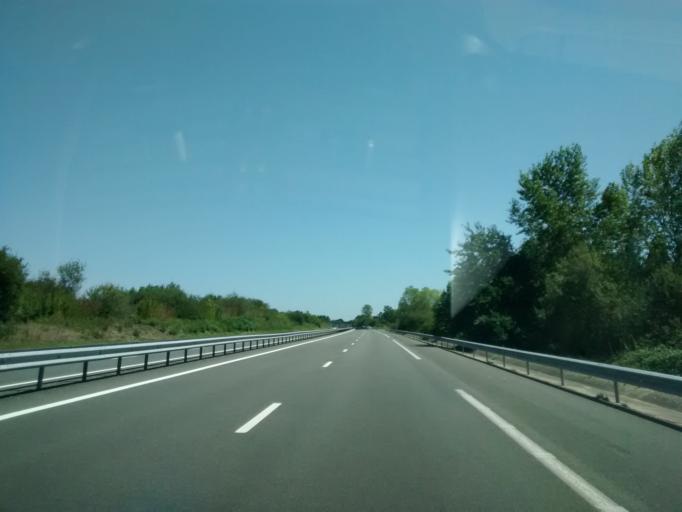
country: FR
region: Aquitaine
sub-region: Departement de la Gironde
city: Saint-Medard-de-Guizieres
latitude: 45.0070
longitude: -0.0623
